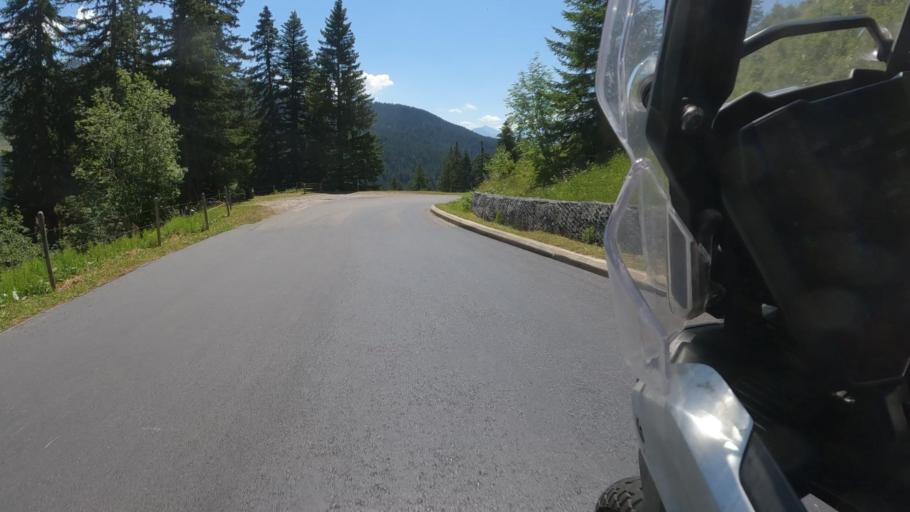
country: CH
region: Vaud
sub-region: Aigle District
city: Villars-sur-Ollon
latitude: 46.3149
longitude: 7.1101
